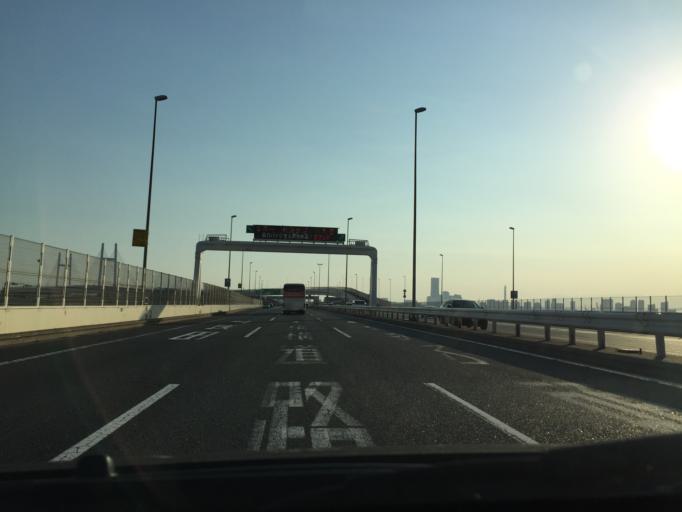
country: JP
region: Kanagawa
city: Yokohama
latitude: 35.4670
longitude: 139.6879
